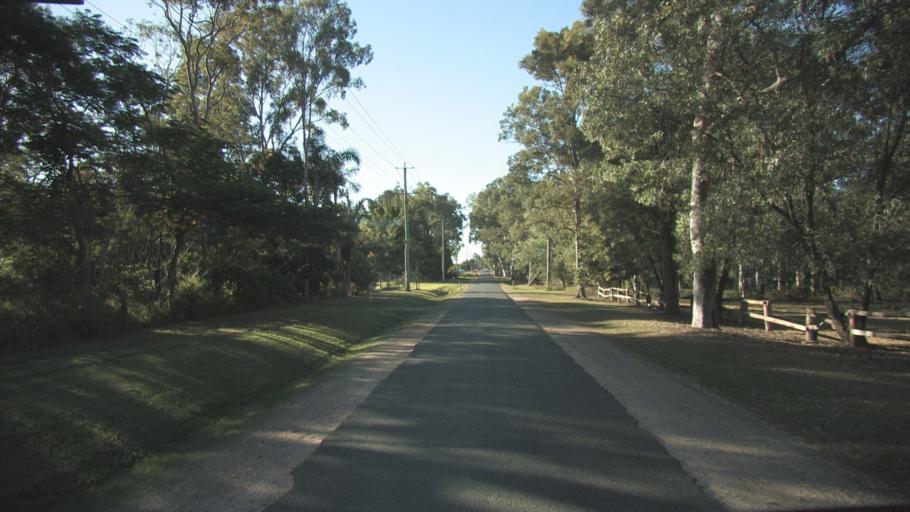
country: AU
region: Queensland
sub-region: Logan
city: Chambers Flat
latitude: -27.7822
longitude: 153.0870
